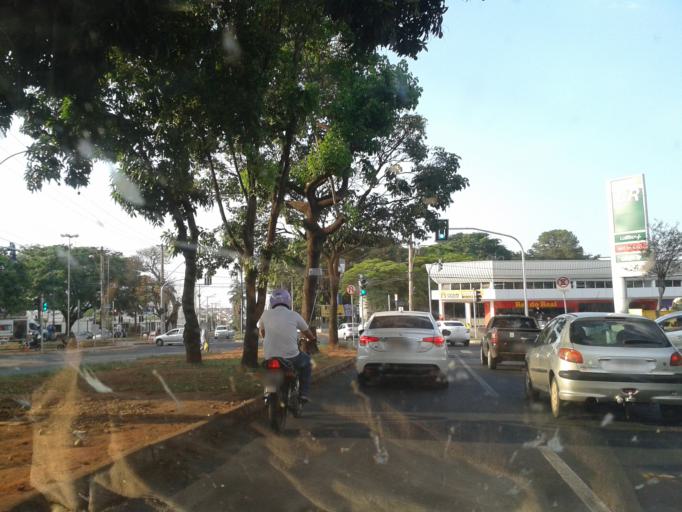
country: BR
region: Minas Gerais
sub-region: Uberlandia
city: Uberlandia
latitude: -18.9299
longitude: -48.3203
